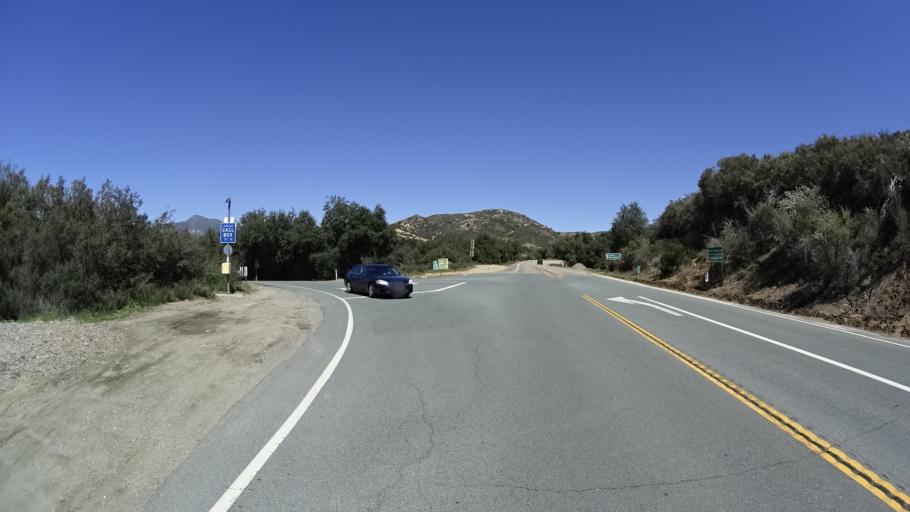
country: US
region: California
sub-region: San Diego County
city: Descanso
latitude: 32.8523
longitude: -116.5947
